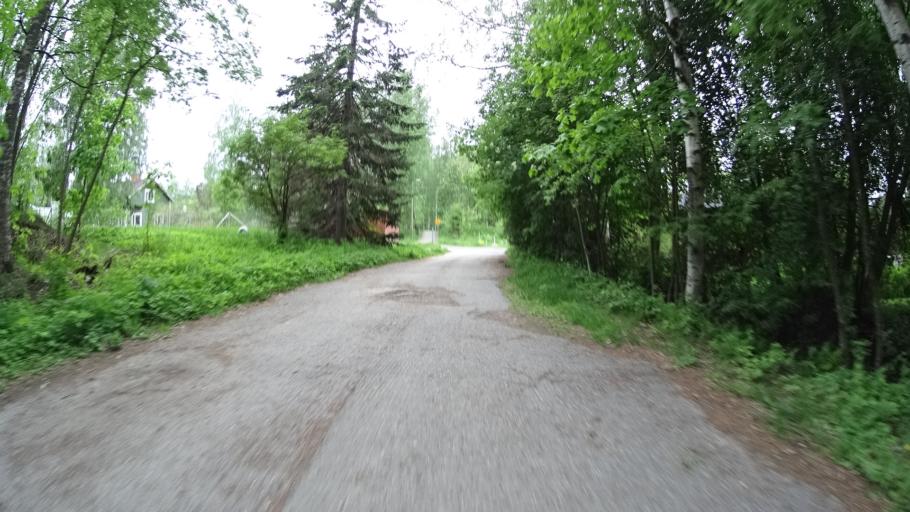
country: FI
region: Uusimaa
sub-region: Helsinki
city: Vantaa
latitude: 60.2197
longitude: 25.0545
